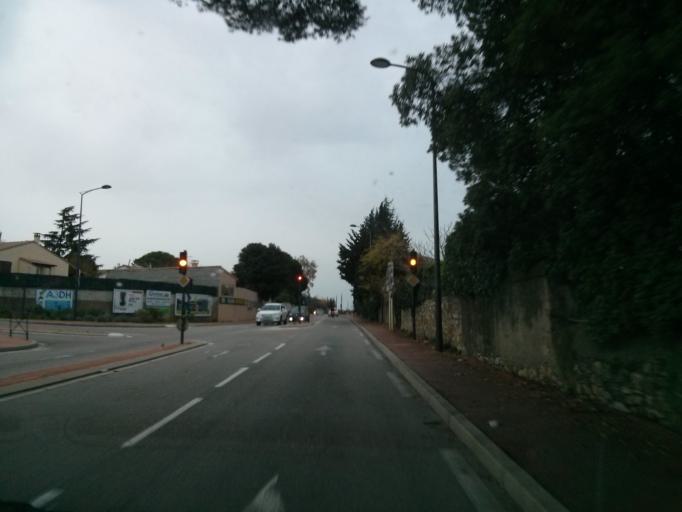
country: FR
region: Languedoc-Roussillon
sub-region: Departement du Gard
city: Caveirac
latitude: 43.8223
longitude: 4.2647
